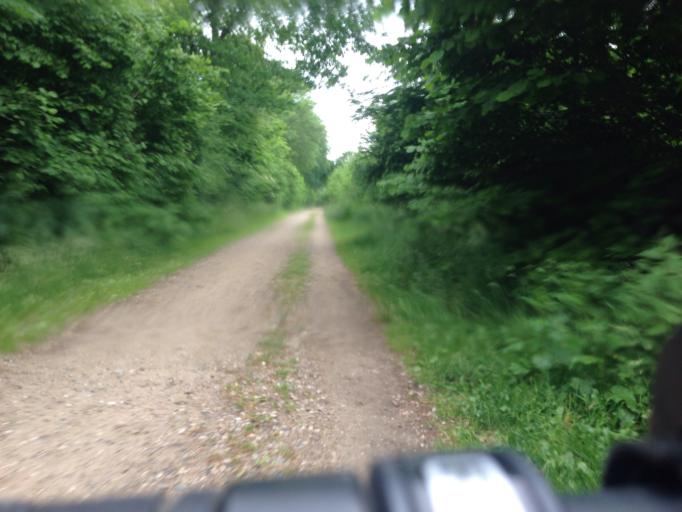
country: DE
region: Schleswig-Holstein
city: Barsbuettel
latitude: 53.5778
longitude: 10.1579
